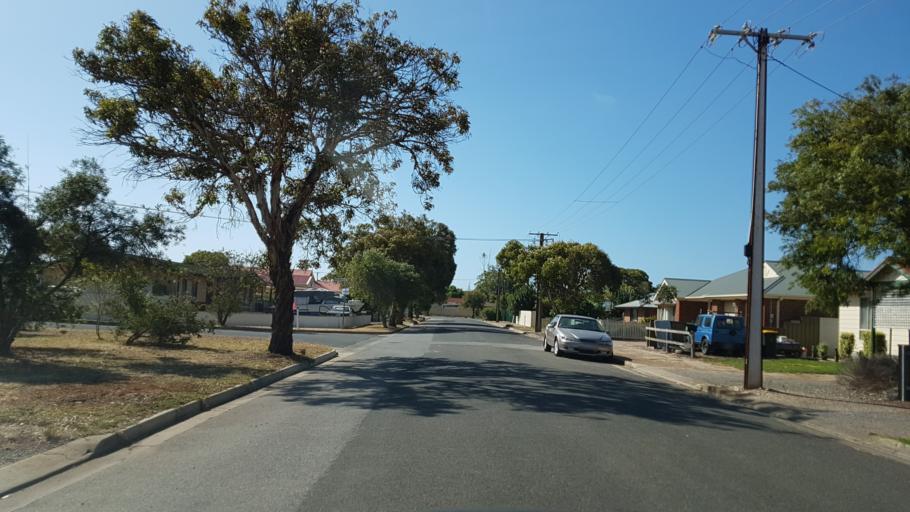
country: AU
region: South Australia
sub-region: Onkaparinga
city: Port Willunga
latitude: -35.2774
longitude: 138.4494
